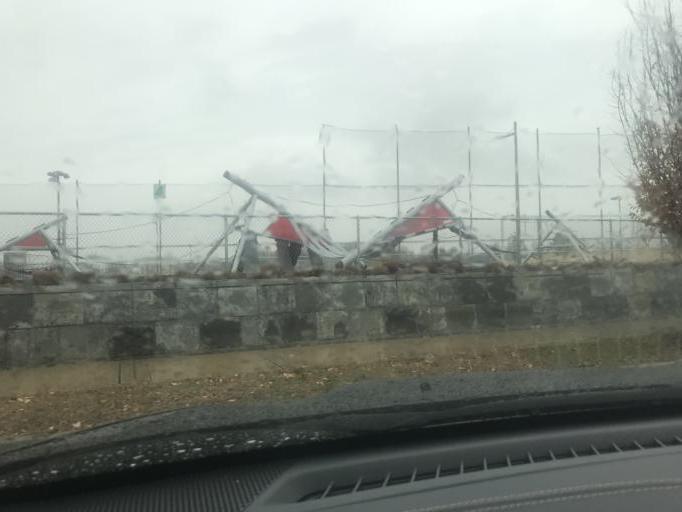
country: US
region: Washington, D.C.
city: Washington, D.C.
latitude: 38.8649
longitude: -77.0487
